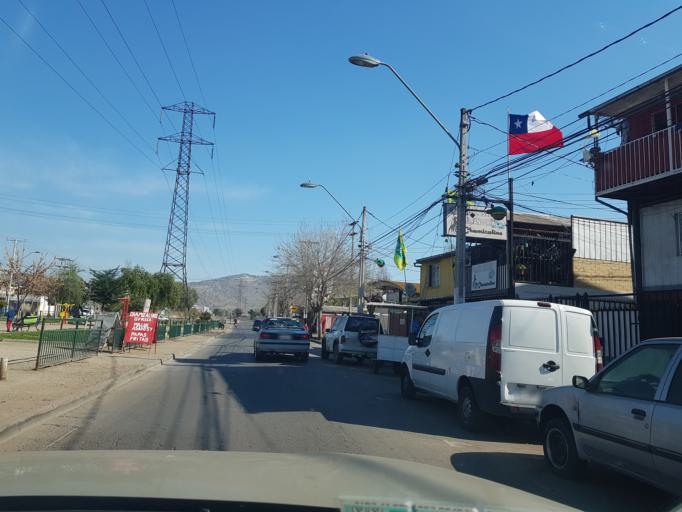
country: CL
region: Santiago Metropolitan
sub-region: Provincia de Santiago
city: Lo Prado
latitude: -33.3707
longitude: -70.7216
